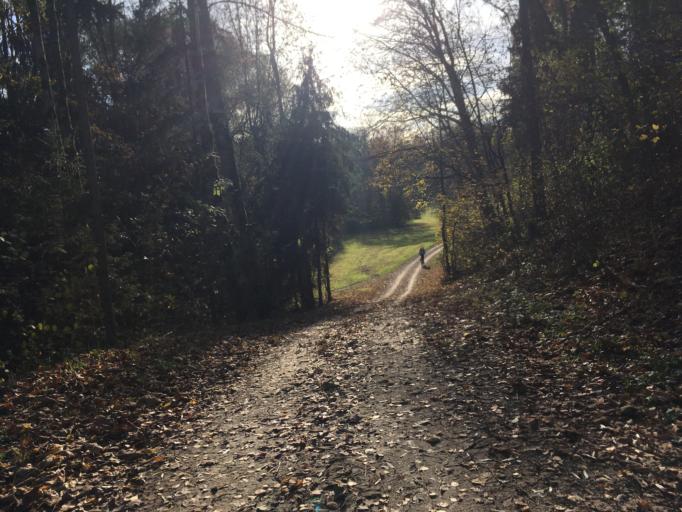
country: DE
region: Baden-Wuerttemberg
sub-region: Regierungsbezirk Stuttgart
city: Neckarwestheim
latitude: 49.0590
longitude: 9.2125
